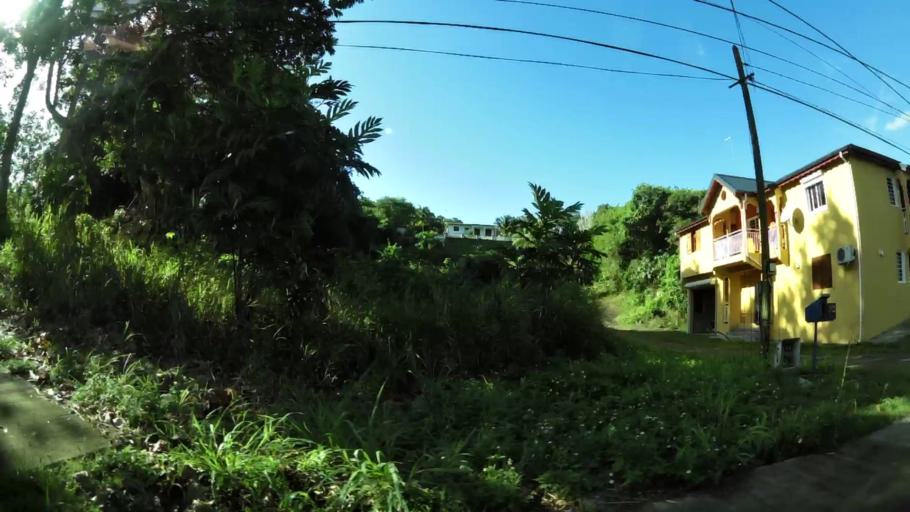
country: GP
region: Guadeloupe
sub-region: Guadeloupe
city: Petit-Canal
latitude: 16.3248
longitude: -61.4441
